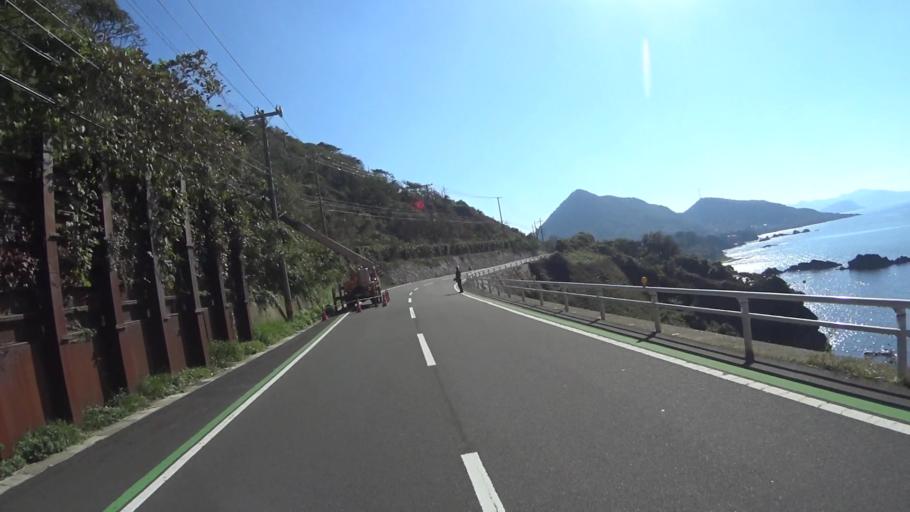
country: JP
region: Kyoto
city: Miyazu
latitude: 35.7284
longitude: 135.0871
